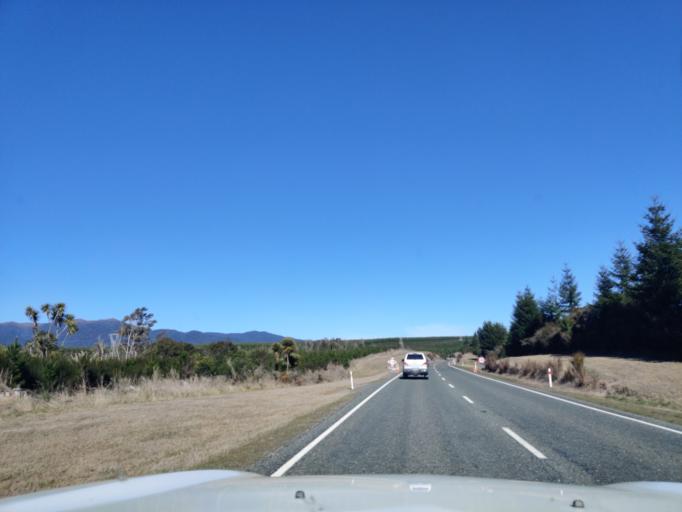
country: NZ
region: Waikato
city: Turangi
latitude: -39.1060
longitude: 175.8079
